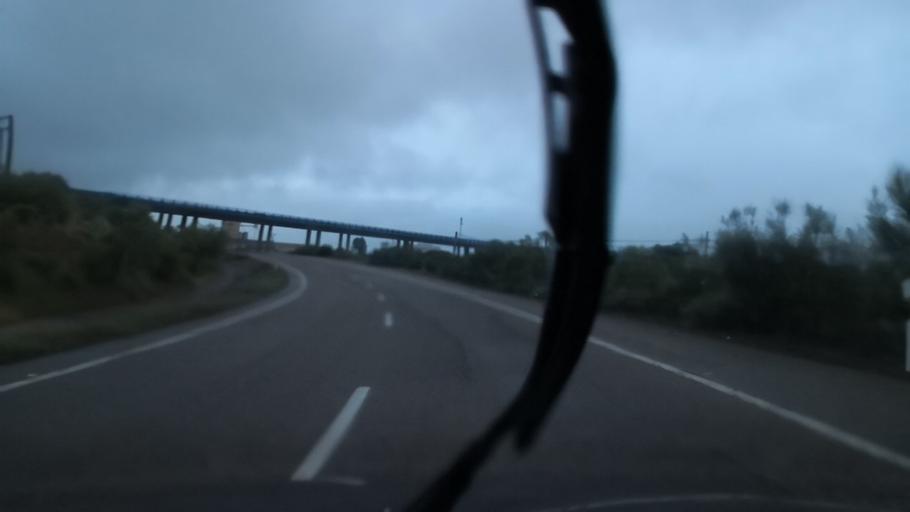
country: ES
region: Extremadura
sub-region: Provincia de Badajoz
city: Calamonte
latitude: 38.9050
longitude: -6.3748
